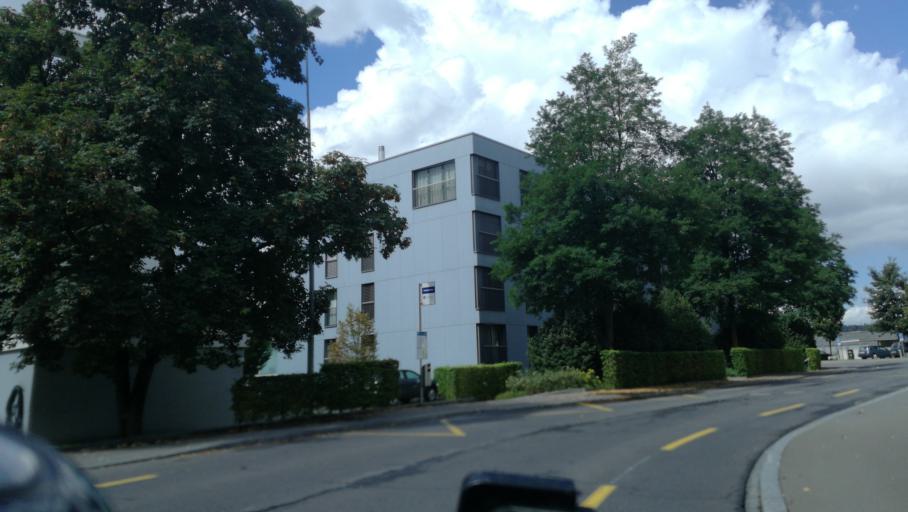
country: CH
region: Zug
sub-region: Zug
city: Zug
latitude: 47.1805
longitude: 8.5110
